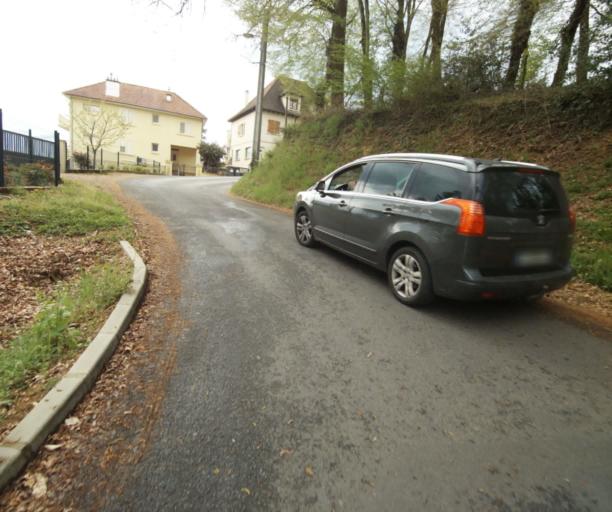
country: FR
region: Limousin
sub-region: Departement de la Correze
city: Tulle
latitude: 45.2653
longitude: 1.7501
